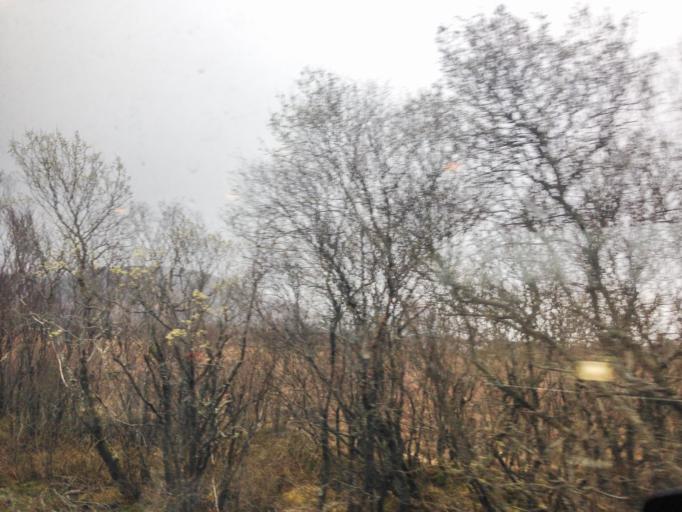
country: GB
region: Scotland
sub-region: Highland
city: Fort William
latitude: 56.8408
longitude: -5.0912
